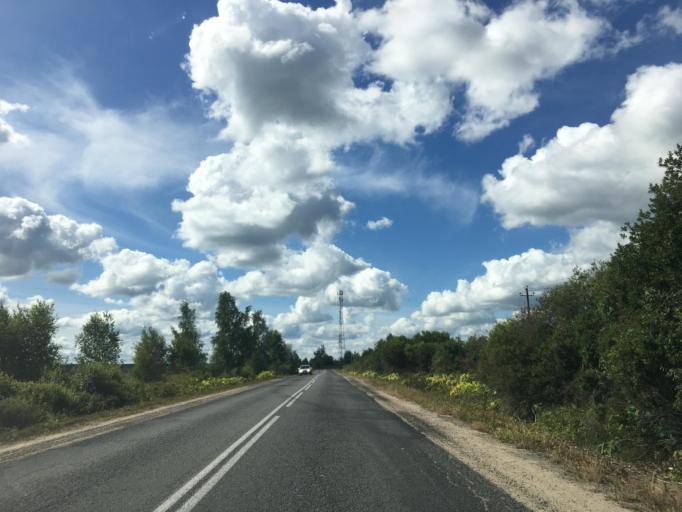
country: RU
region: Pskov
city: Pskov
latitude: 57.7406
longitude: 28.1572
